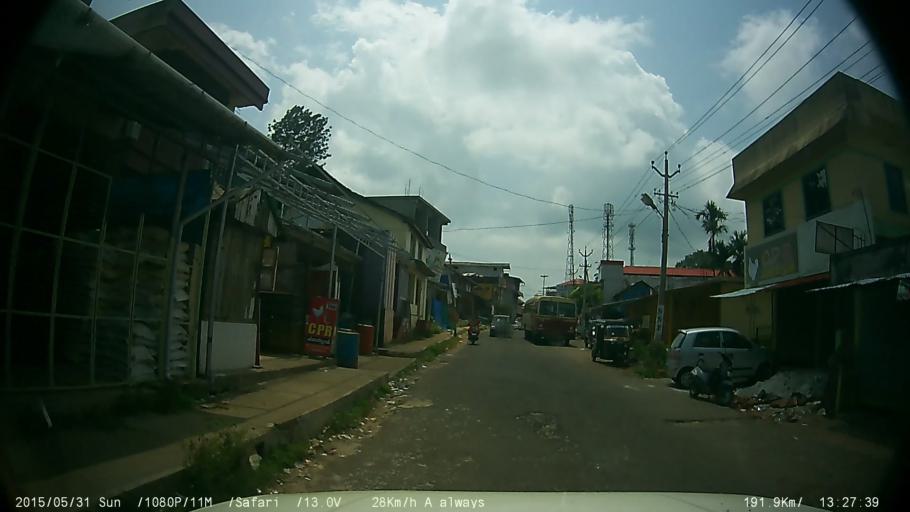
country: IN
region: Kerala
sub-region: Wayanad
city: Kalpetta
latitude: 11.5516
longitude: 76.1331
